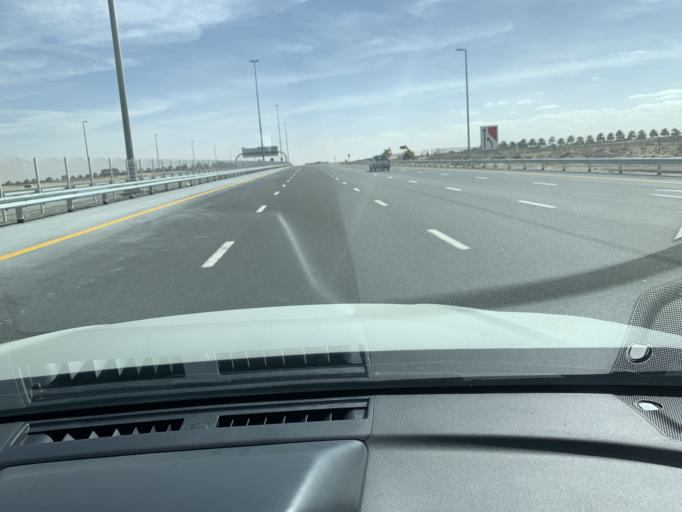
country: AE
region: Dubai
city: Dubai
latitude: 24.9515
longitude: 55.2448
